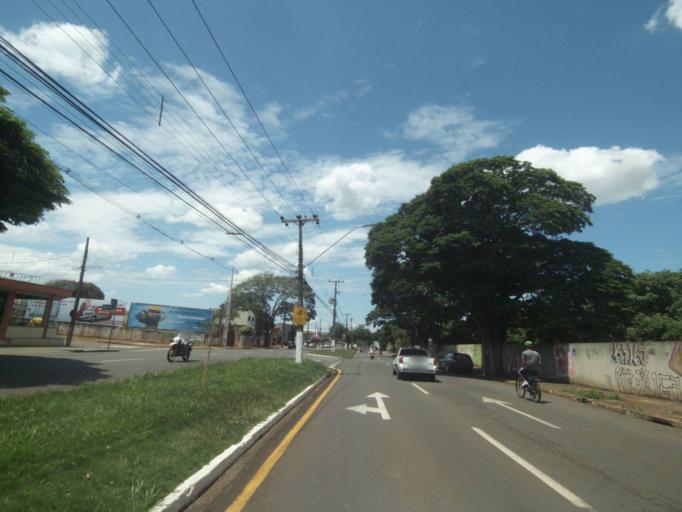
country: BR
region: Parana
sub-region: Londrina
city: Londrina
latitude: -23.3070
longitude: -51.2007
